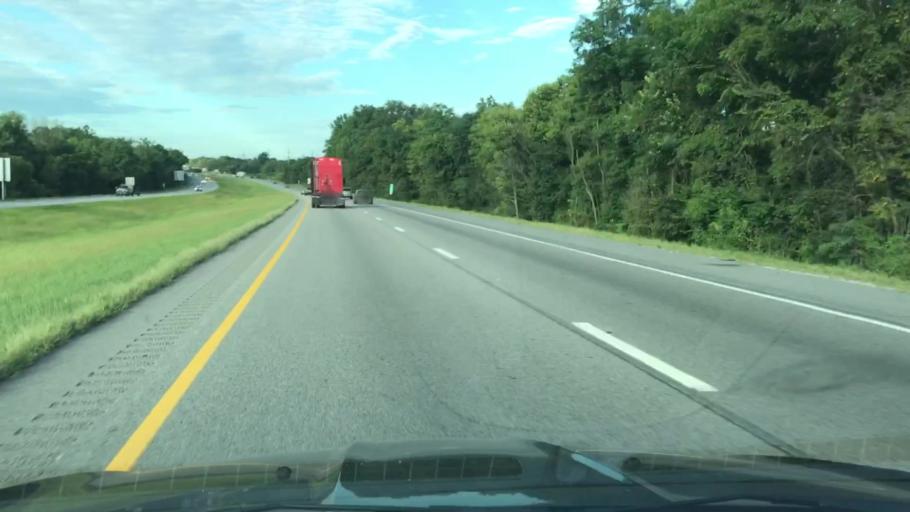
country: US
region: Pennsylvania
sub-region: Cumberland County
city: Mechanicsburg
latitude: 40.2636
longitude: -77.0571
